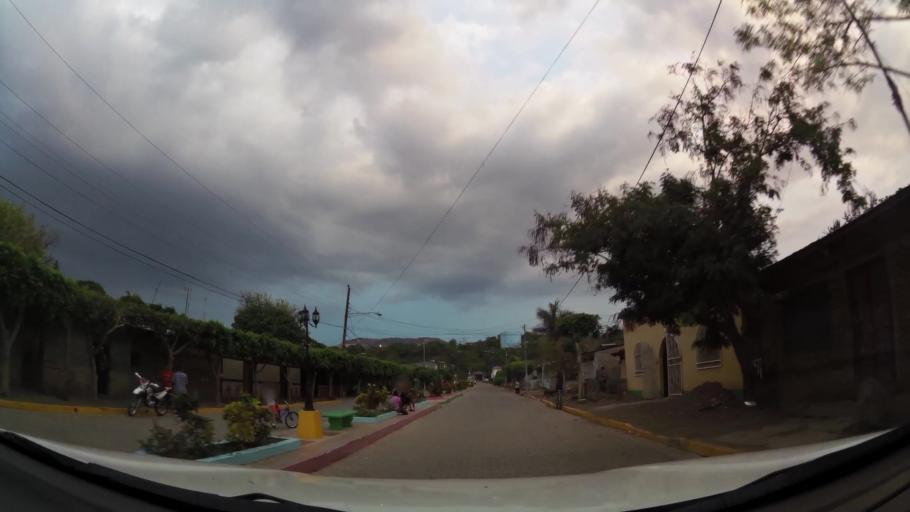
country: NI
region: Matagalpa
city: Ciudad Dario
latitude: 12.8486
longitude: -86.0959
